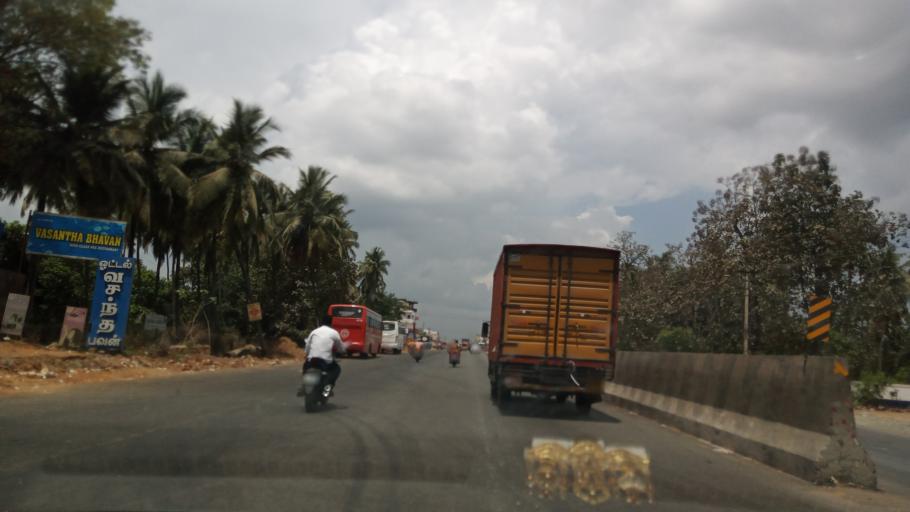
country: IN
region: Tamil Nadu
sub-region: Kancheepuram
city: Madambakkam
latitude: 12.8889
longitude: 80.0303
